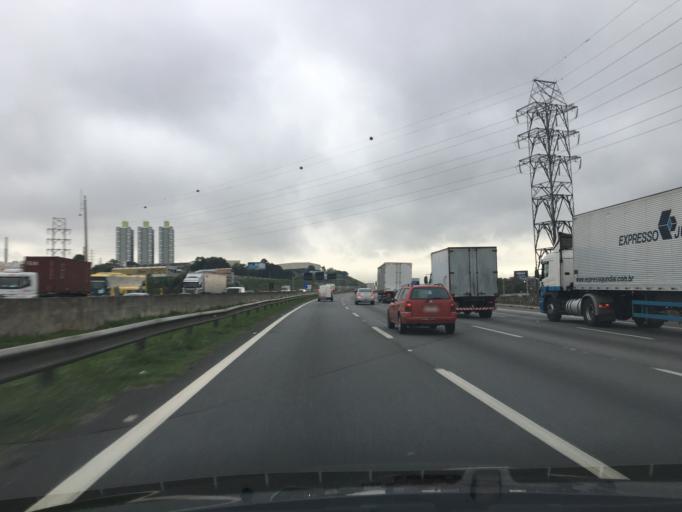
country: BR
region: Sao Paulo
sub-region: Carapicuiba
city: Carapicuiba
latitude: -23.5384
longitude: -46.8178
